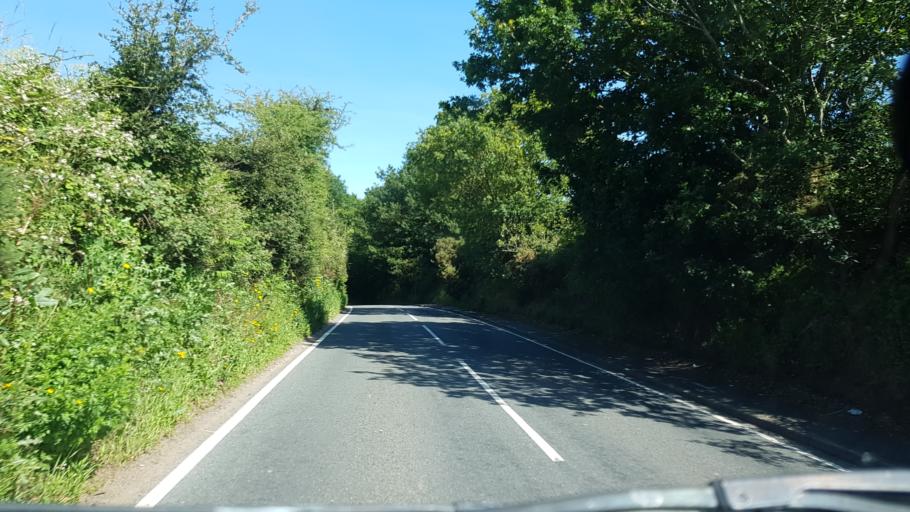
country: GB
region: England
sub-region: Worcestershire
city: Bewdley
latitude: 52.3600
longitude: -2.3009
